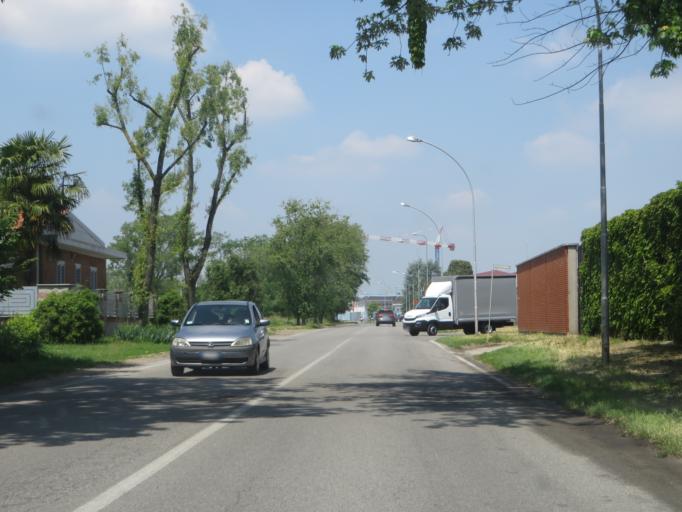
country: IT
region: Lombardy
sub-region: Citta metropolitana di Milano
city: Bareggio
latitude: 45.4904
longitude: 8.9957
